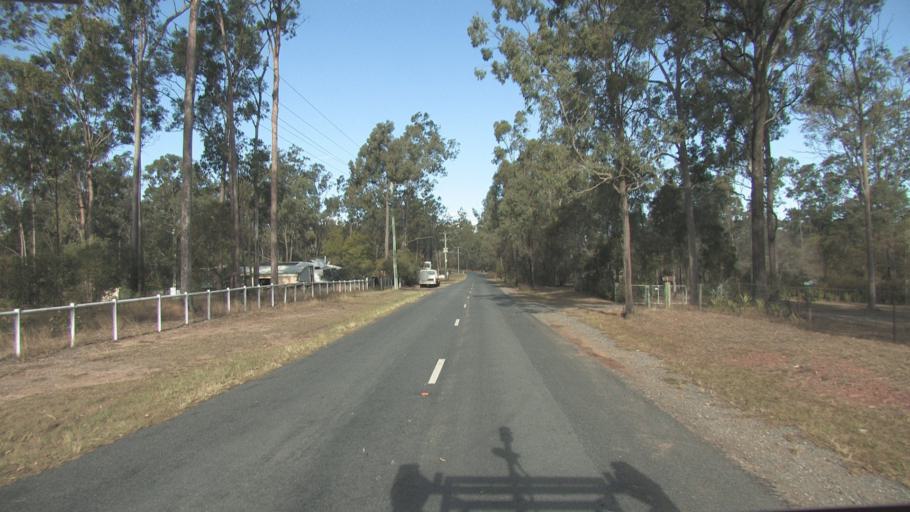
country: AU
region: Queensland
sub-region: Logan
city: Cedar Vale
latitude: -27.8434
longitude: 153.0568
